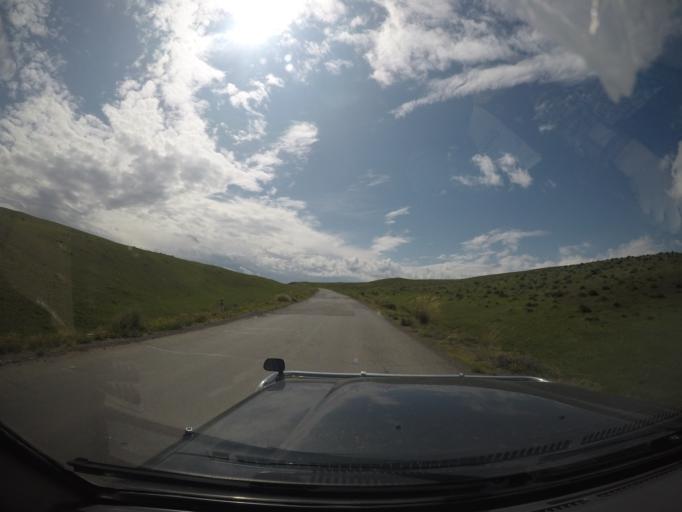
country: MN
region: Hentiy
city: Bayanbulag
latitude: 47.4462
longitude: 109.7737
